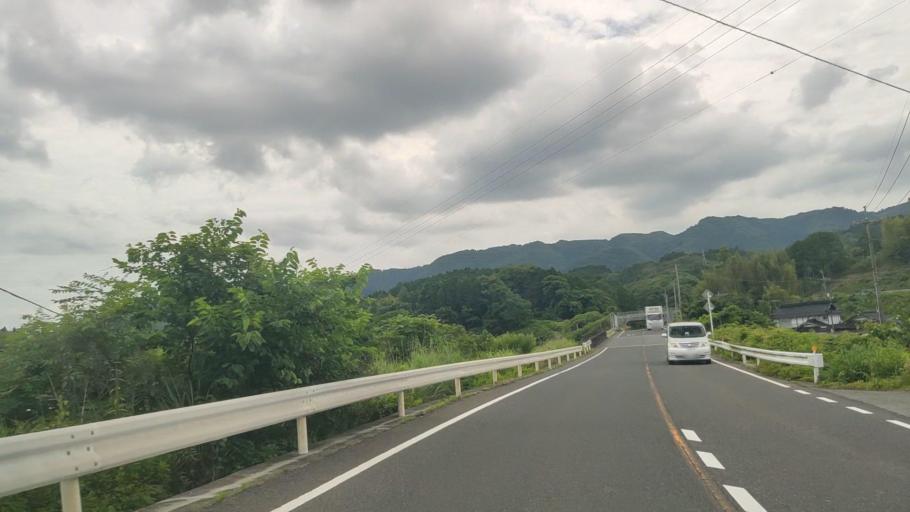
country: JP
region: Okayama
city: Tsuyama
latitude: 35.0646
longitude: 133.8563
